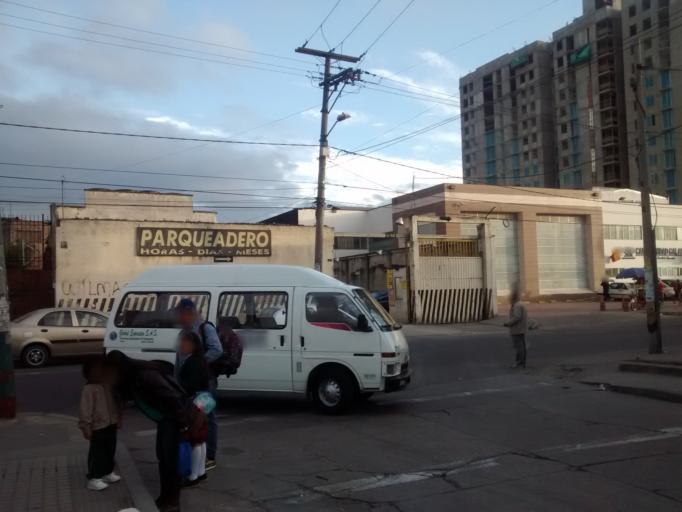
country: CO
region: Bogota D.C.
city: Bogota
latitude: 4.6219
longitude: -74.1205
